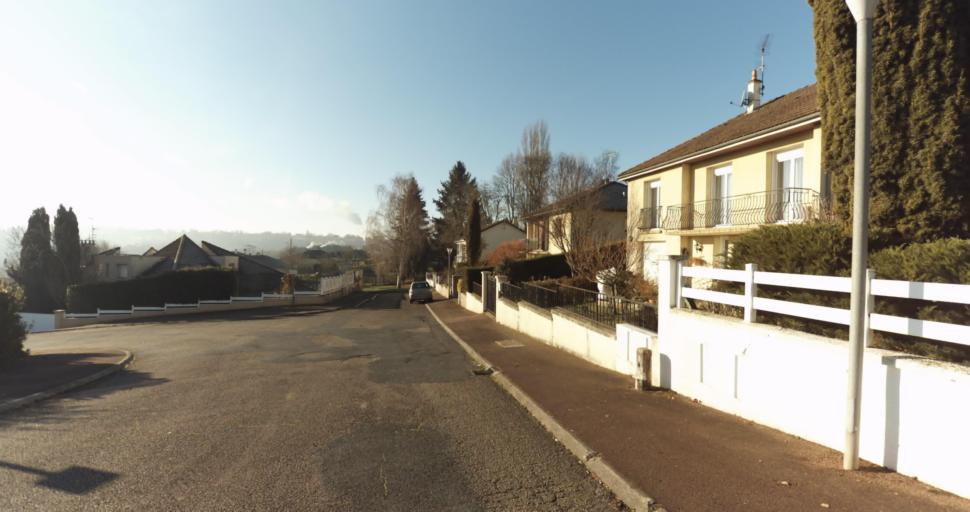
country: FR
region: Limousin
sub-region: Departement de la Haute-Vienne
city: Aixe-sur-Vienne
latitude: 45.8015
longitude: 1.1514
